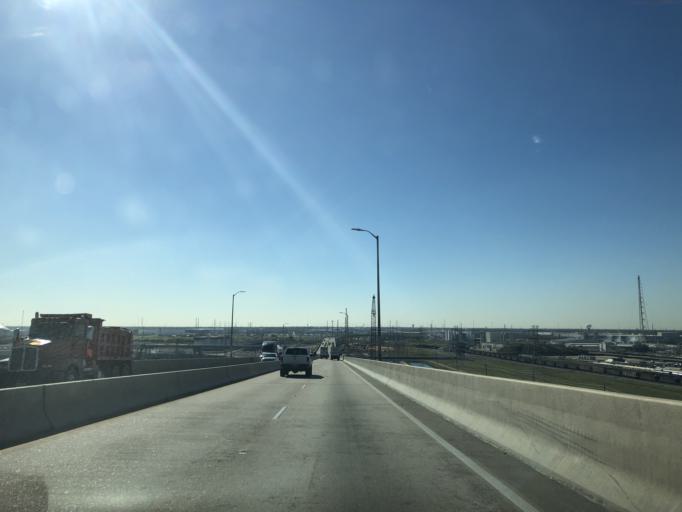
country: US
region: Texas
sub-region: Harris County
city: Deer Park
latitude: 29.7304
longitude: -95.1469
